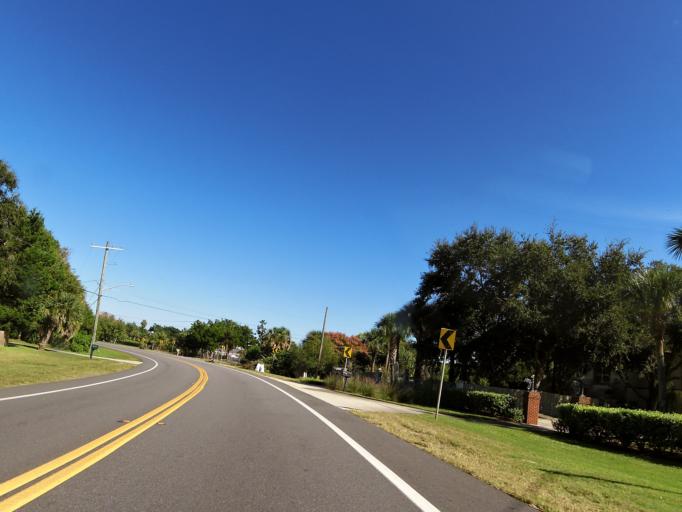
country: US
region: Florida
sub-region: Duval County
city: Atlantic Beach
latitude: 30.3849
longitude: -81.4489
